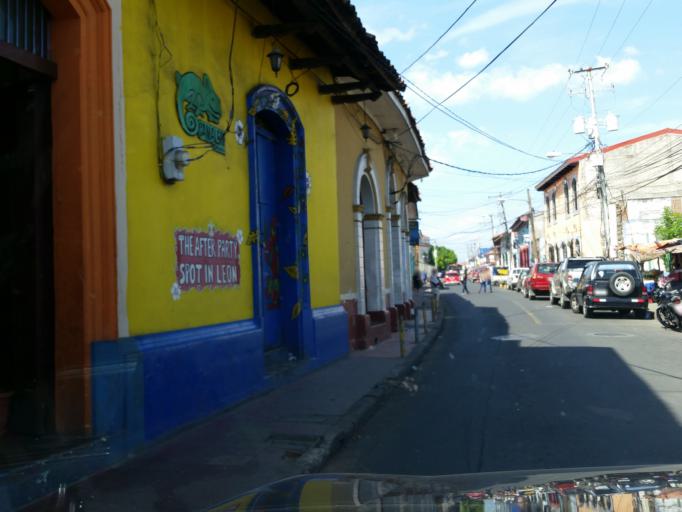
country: NI
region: Leon
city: Leon
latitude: 12.4371
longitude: -86.8785
